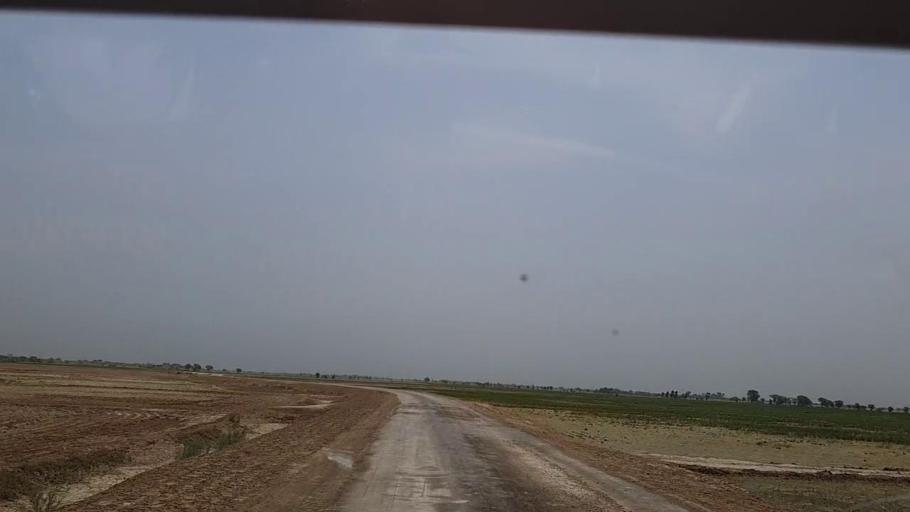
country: PK
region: Sindh
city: Khairpur Nathan Shah
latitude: 27.0180
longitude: 67.6457
